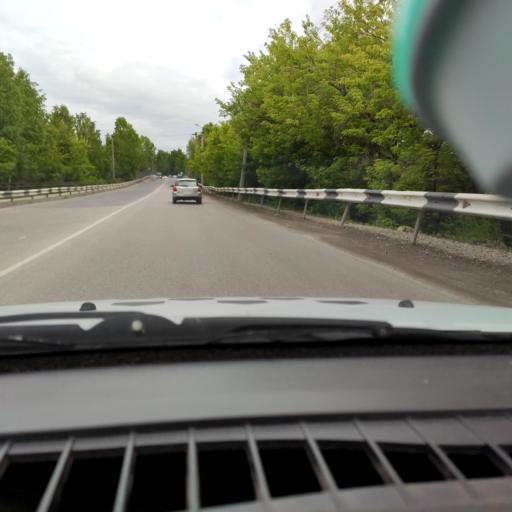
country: RU
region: Perm
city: Chusovoy
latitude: 58.2826
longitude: 57.8130
